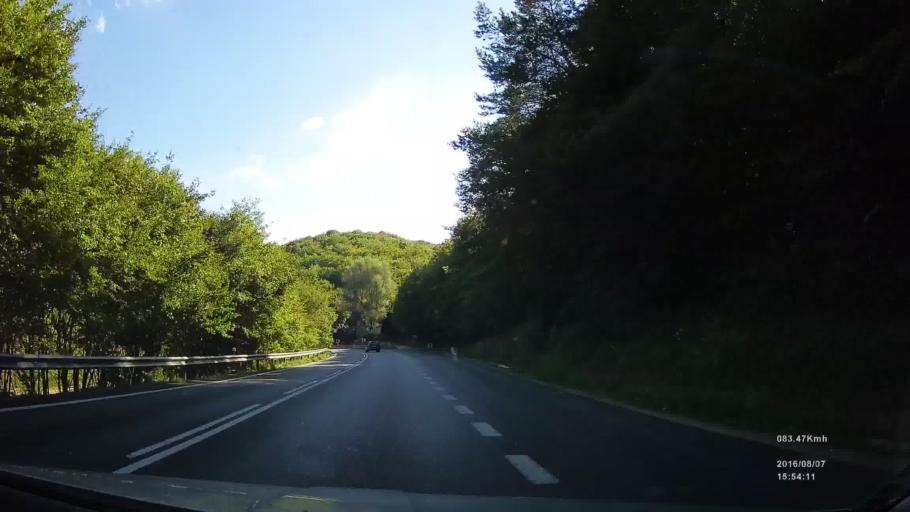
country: SK
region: Presovsky
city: Giraltovce
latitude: 49.0904
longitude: 21.4443
